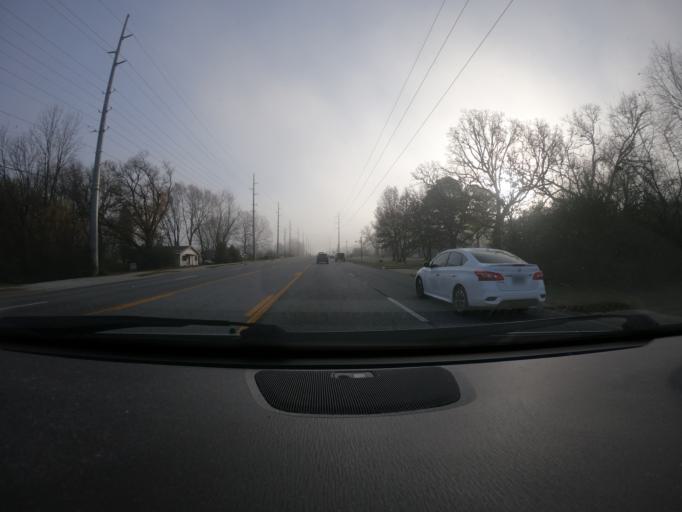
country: US
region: Arkansas
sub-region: Benton County
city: Bentonville
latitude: 36.3575
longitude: -94.2366
